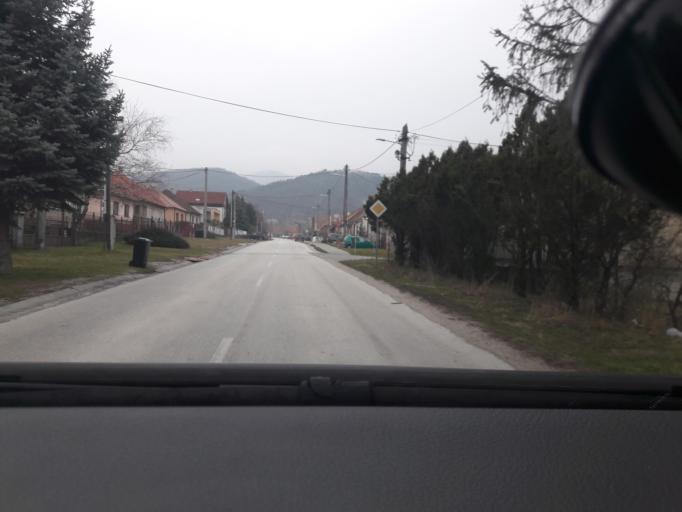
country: SK
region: Trnavsky
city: Smolenice
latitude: 48.5040
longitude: 17.4371
